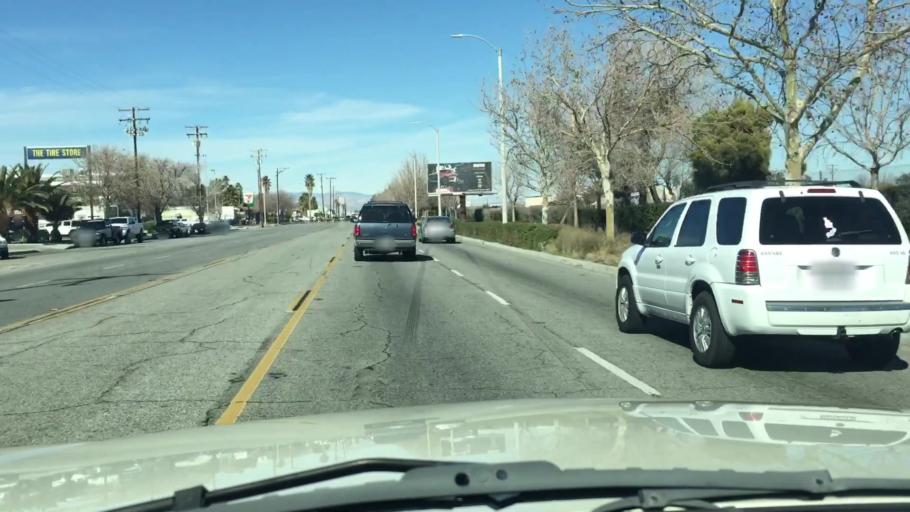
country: US
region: California
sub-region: Los Angeles County
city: Lancaster
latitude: 34.6806
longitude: -118.1337
